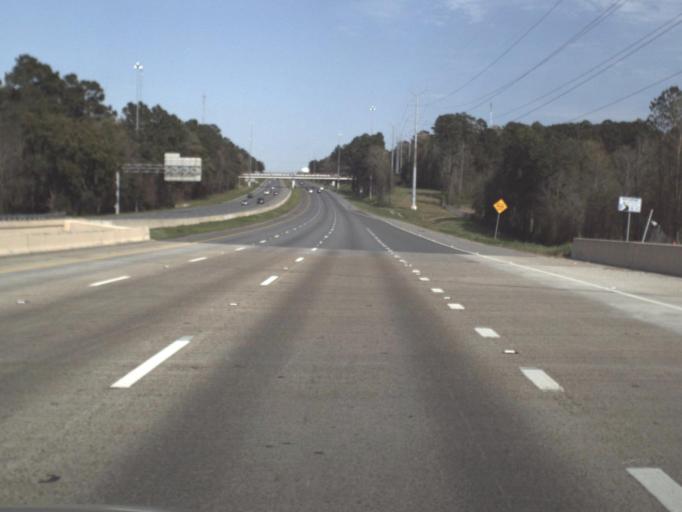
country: US
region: Florida
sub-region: Leon County
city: Tallahassee
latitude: 30.4845
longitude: -84.3011
